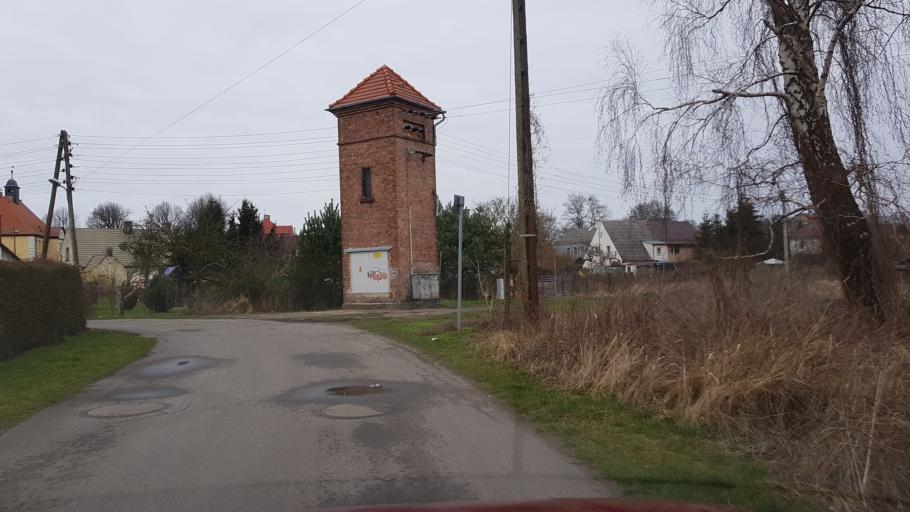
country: PL
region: West Pomeranian Voivodeship
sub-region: Powiat goleniowski
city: Stepnica
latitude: 53.6563
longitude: 14.5130
